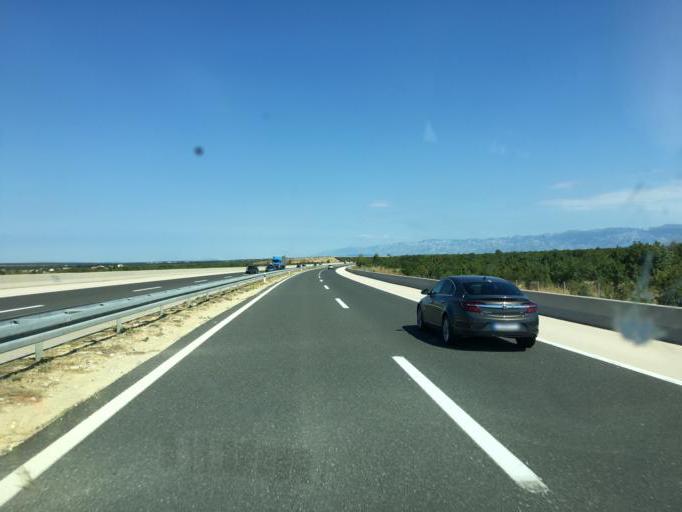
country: HR
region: Zadarska
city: Galovac
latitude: 44.1277
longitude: 15.4256
